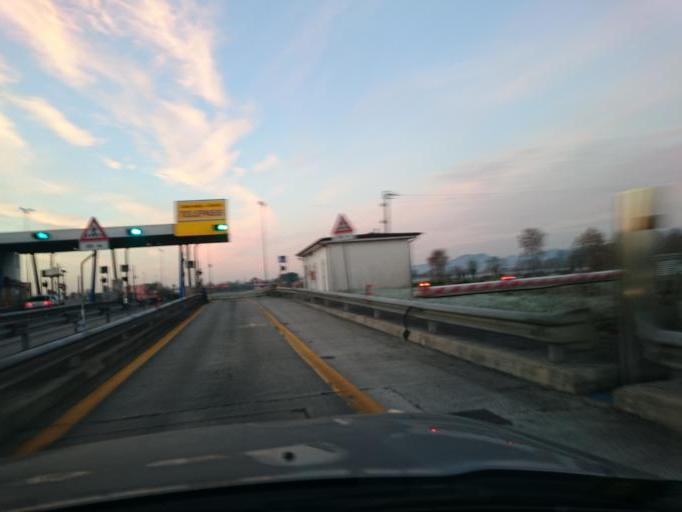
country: IT
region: Veneto
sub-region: Provincia di Padova
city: Mandriola-Sant'Agostino
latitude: 45.3452
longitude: 11.8480
